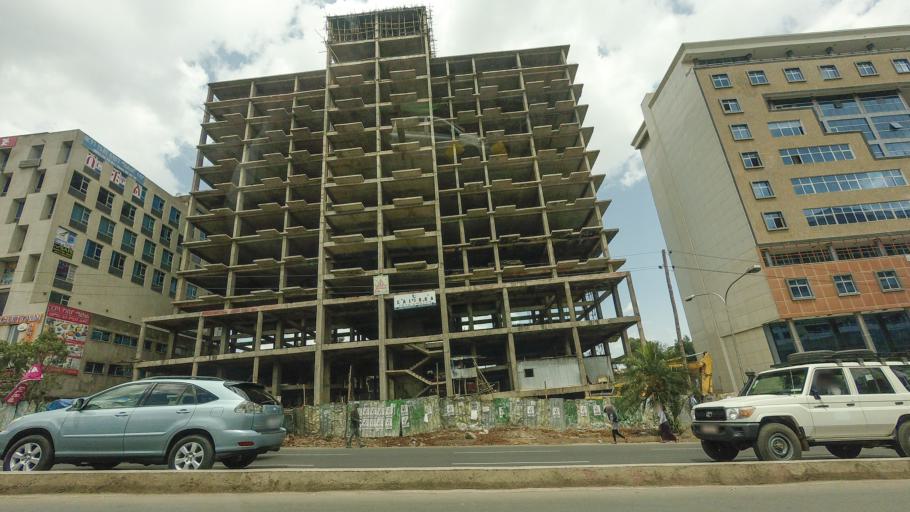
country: ET
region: Adis Abeba
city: Addis Ababa
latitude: 9.0307
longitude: 38.7512
